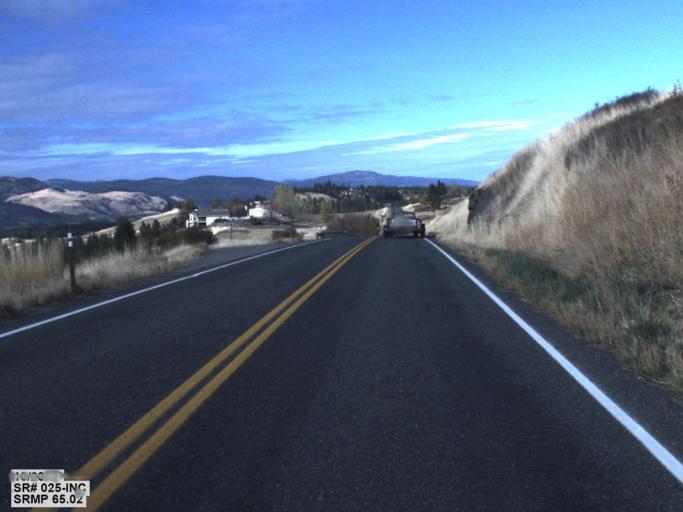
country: US
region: Washington
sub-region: Stevens County
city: Kettle Falls
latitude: 48.4100
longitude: -118.1716
